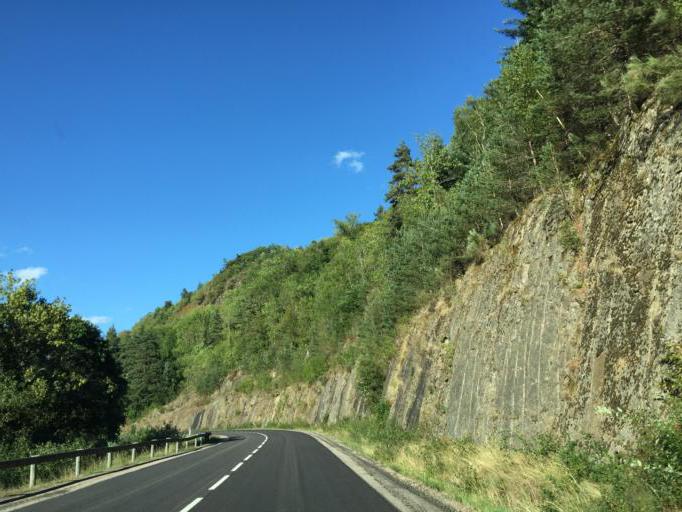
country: FR
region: Auvergne
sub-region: Departement de la Haute-Loire
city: Saugues
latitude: 44.9595
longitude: 3.6290
